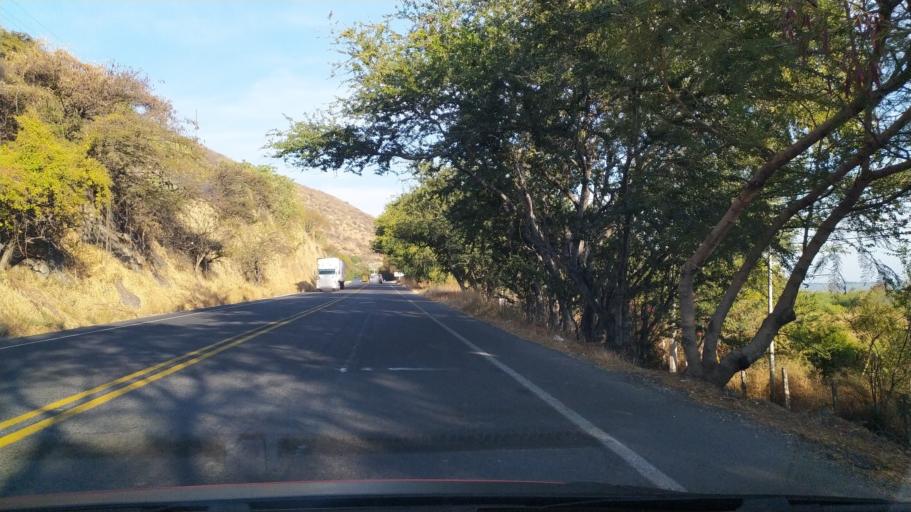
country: MX
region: Jalisco
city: Jamay
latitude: 20.2935
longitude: -102.7417
